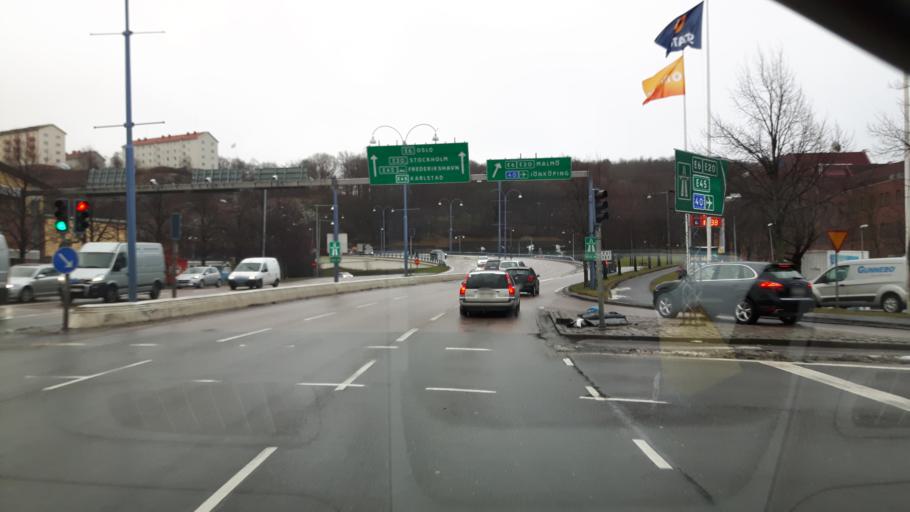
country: SE
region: Vaestra Goetaland
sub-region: Goteborg
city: Goeteborg
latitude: 57.7075
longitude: 11.9920
